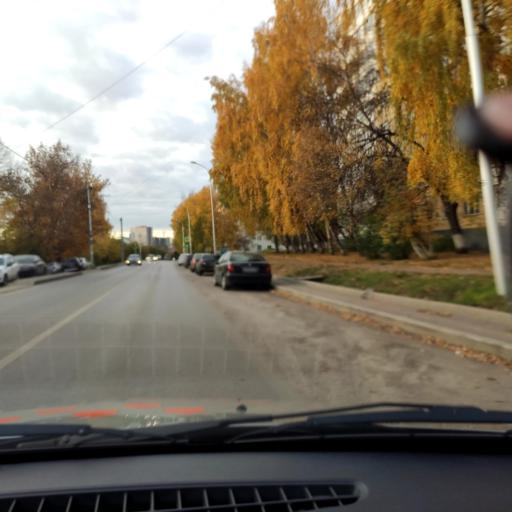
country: RU
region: Bashkortostan
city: Ufa
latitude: 54.7373
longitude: 56.0001
